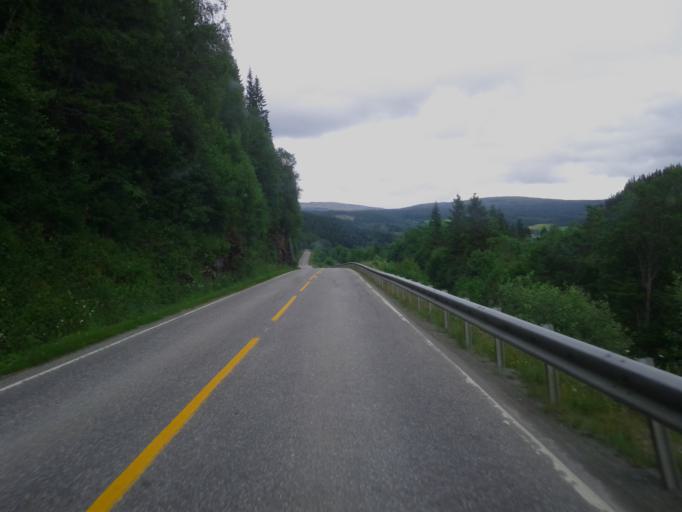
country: NO
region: Sor-Trondelag
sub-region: Klaebu
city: Klaebu
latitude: 62.9449
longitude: 10.6774
